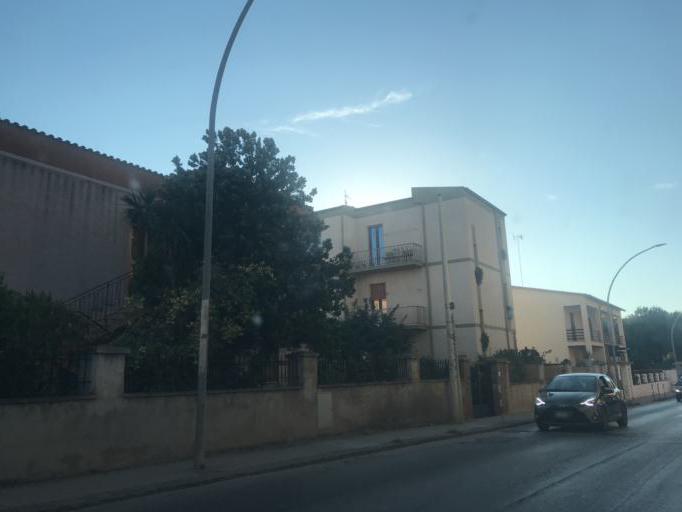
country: IT
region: Sardinia
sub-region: Provincia di Sassari
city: Alghero
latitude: 40.5705
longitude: 8.3253
